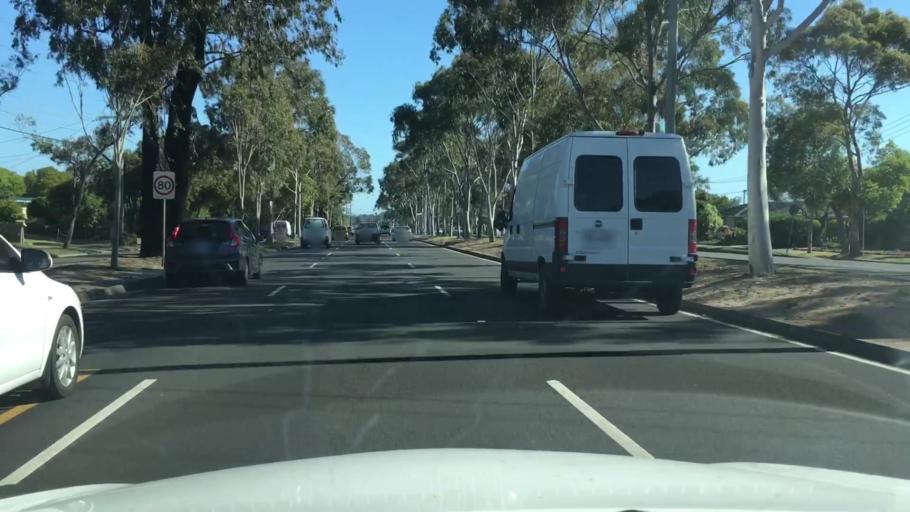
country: AU
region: Victoria
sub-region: Monash
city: Notting Hill
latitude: -37.8990
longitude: 145.1625
